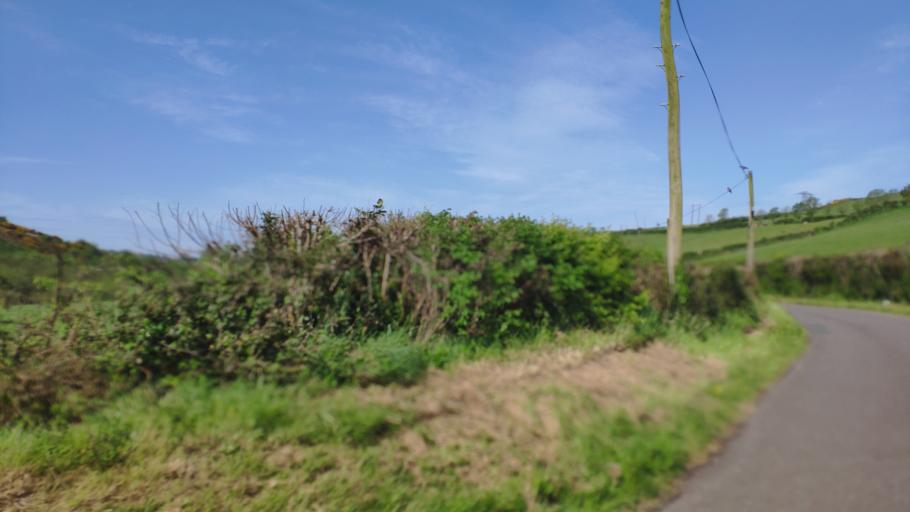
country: IE
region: Munster
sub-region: County Cork
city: Cork
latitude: 51.9176
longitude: -8.5097
